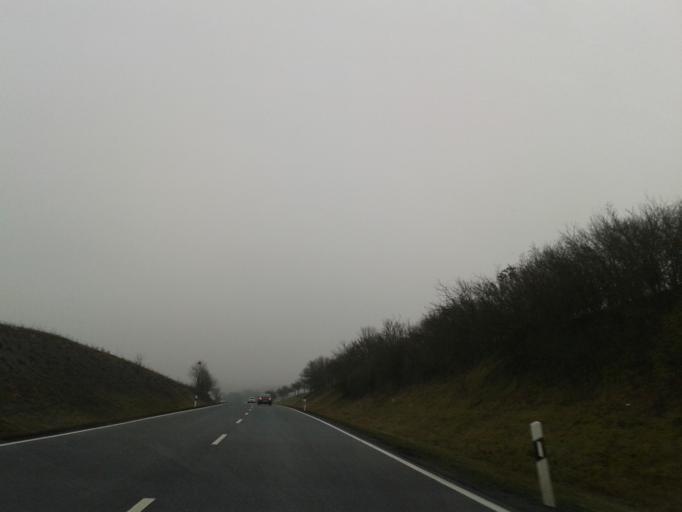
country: DE
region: Bavaria
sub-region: Regierungsbezirk Unterfranken
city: Hofheim in Unterfranken
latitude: 50.1252
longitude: 10.5462
